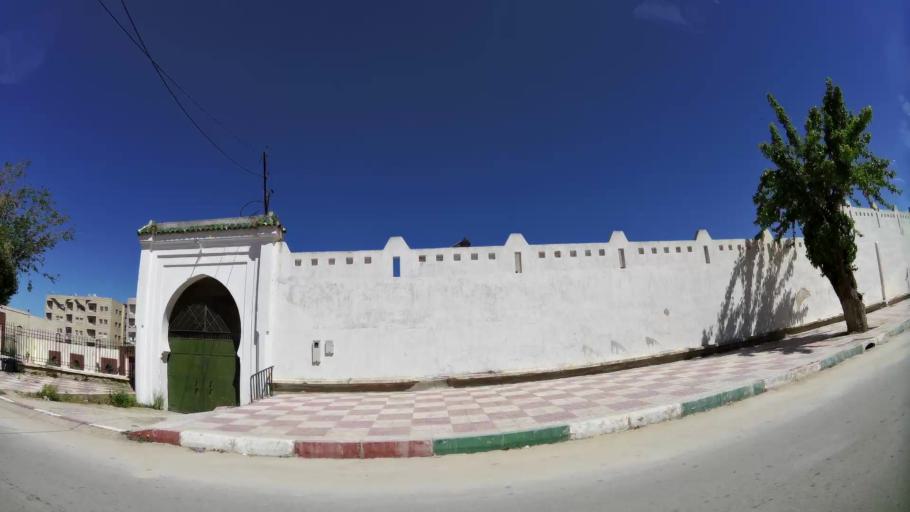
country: MA
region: Meknes-Tafilalet
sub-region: Meknes
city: Meknes
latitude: 33.8934
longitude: -5.5766
